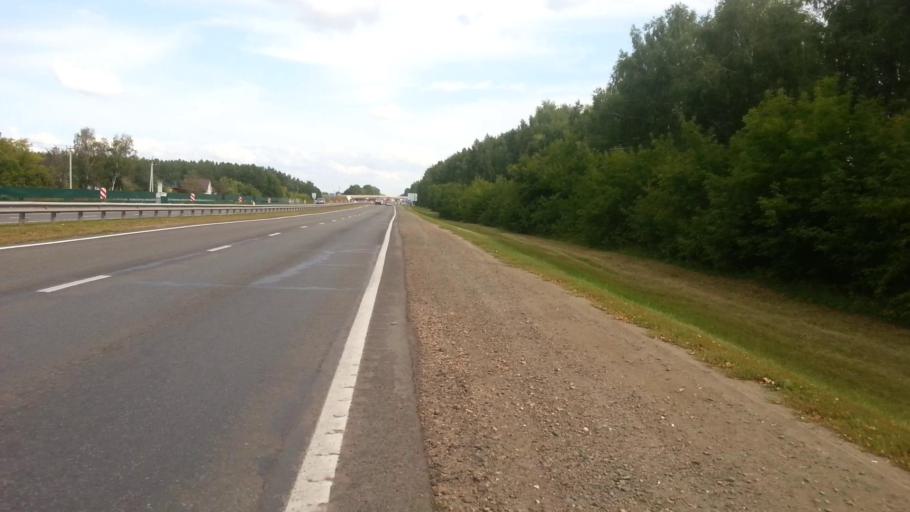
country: RU
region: Altai Krai
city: Vlasikha
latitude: 53.3542
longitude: 83.5437
